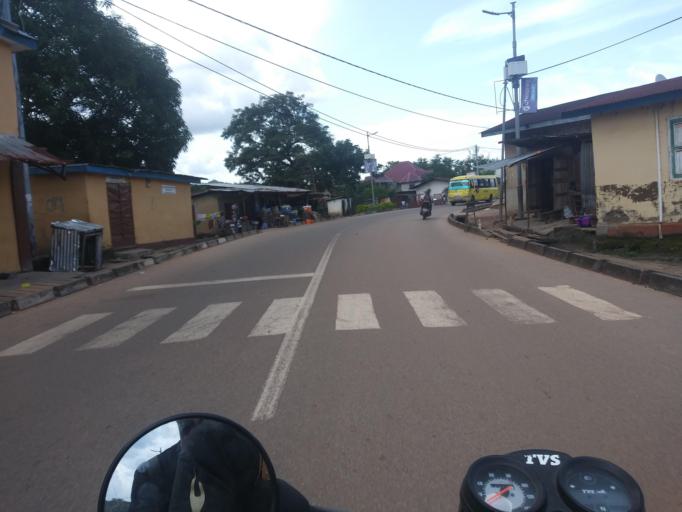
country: SL
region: Northern Province
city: Makeni
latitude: 8.8784
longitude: -12.0449
